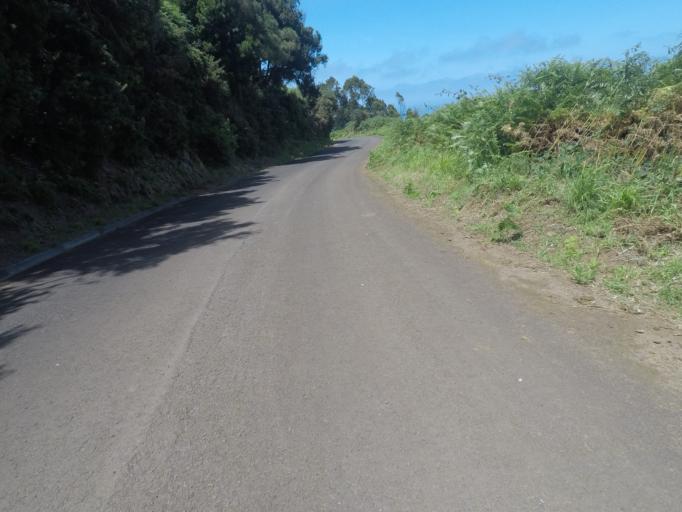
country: PT
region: Madeira
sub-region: Porto Moniz
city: Porto Moniz
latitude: 32.8439
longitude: -17.1504
